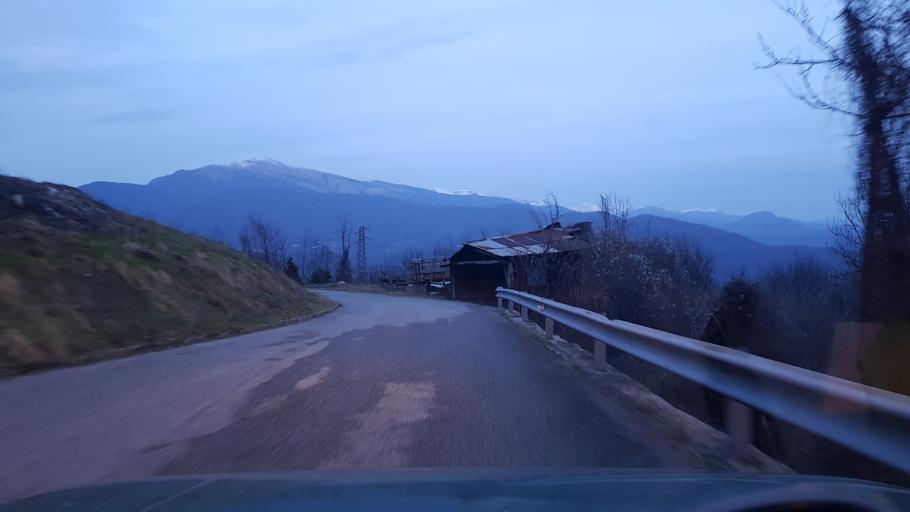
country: IT
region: Friuli Venezia Giulia
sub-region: Provincia di Udine
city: Pulfero
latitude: 46.1477
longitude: 13.4646
